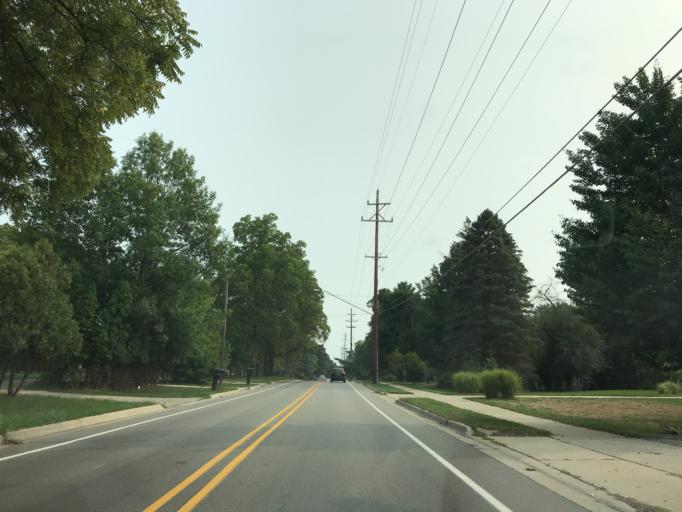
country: US
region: Michigan
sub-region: Ingham County
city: Okemos
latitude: 42.7369
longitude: -84.4475
